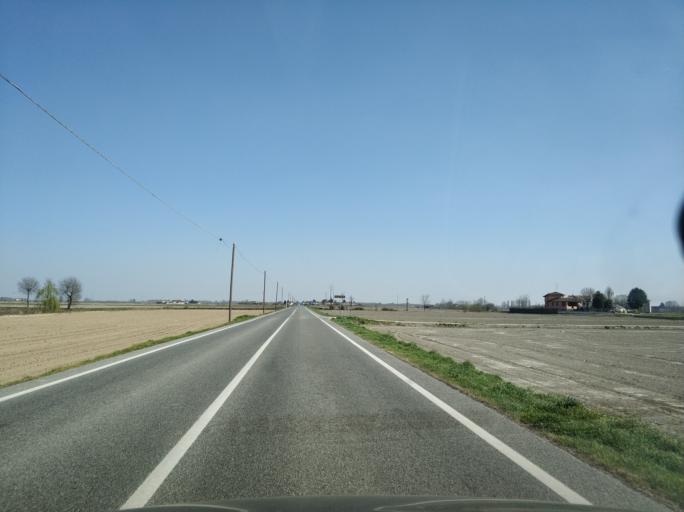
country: IT
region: Piedmont
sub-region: Provincia di Vercelli
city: Borgo Vercelli
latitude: 45.3216
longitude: 8.4800
